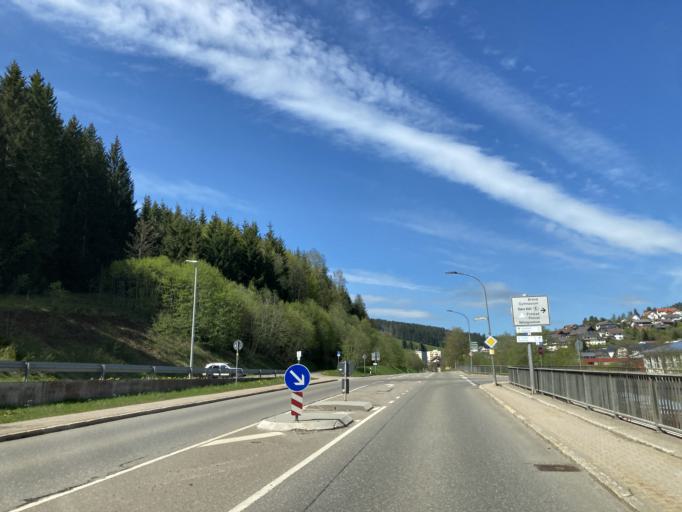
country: DE
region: Baden-Wuerttemberg
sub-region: Freiburg Region
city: Furtwangen im Schwarzwald
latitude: 48.0474
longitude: 8.2034
